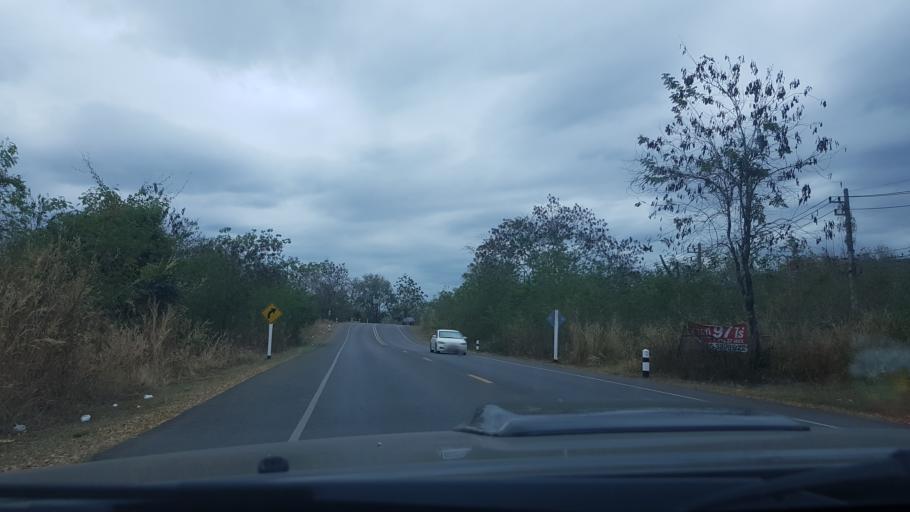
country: TH
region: Phetchabun
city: Phetchabun
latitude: 16.5372
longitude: 101.1140
